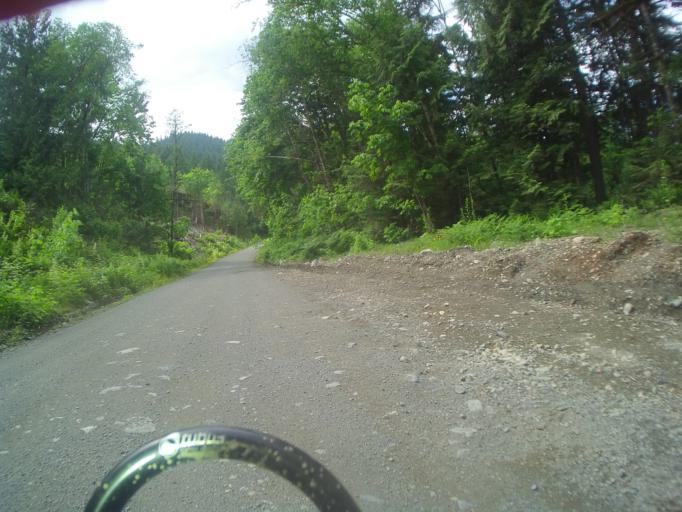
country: CA
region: British Columbia
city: Agassiz
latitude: 49.5936
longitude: -121.9317
